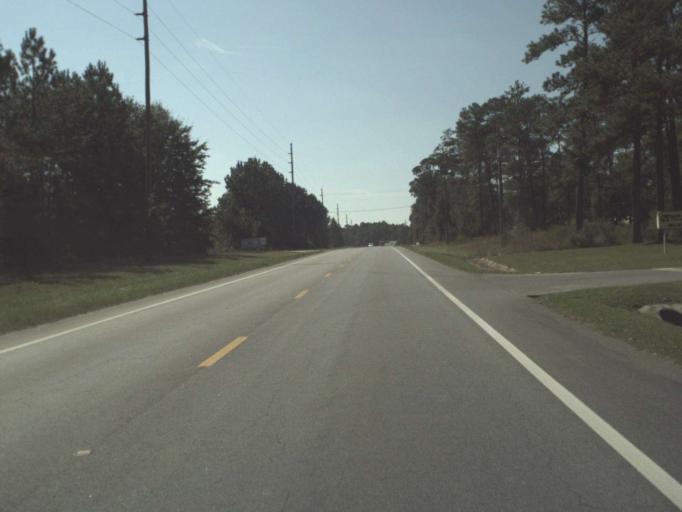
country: US
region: Florida
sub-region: Liberty County
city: Bristol
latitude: 30.3706
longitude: -84.8107
